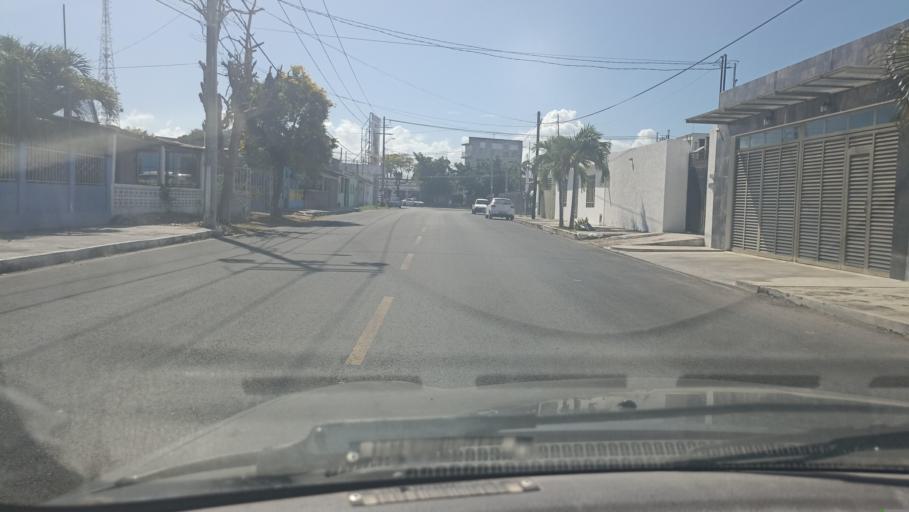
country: MX
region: Quintana Roo
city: Chetumal
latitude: 18.5081
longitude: -88.2917
